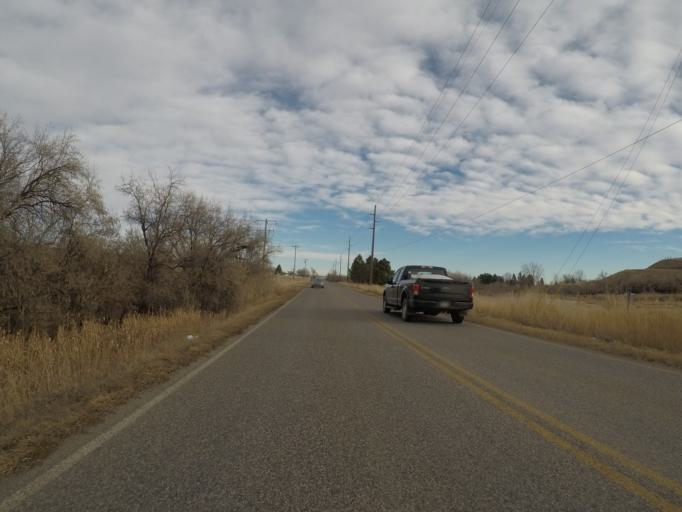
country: US
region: Montana
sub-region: Yellowstone County
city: Laurel
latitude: 45.7840
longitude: -108.6988
